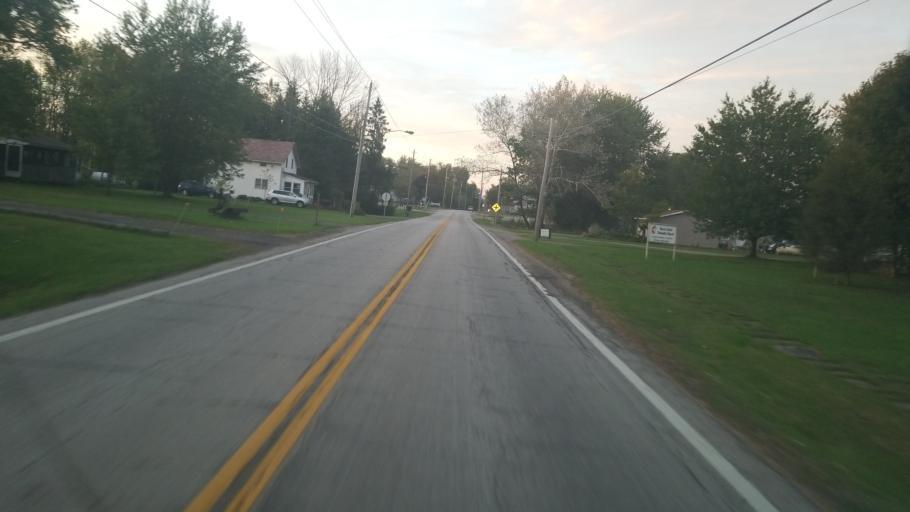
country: US
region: Ohio
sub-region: Ashtabula County
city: Andover
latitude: 41.6750
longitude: -80.6677
